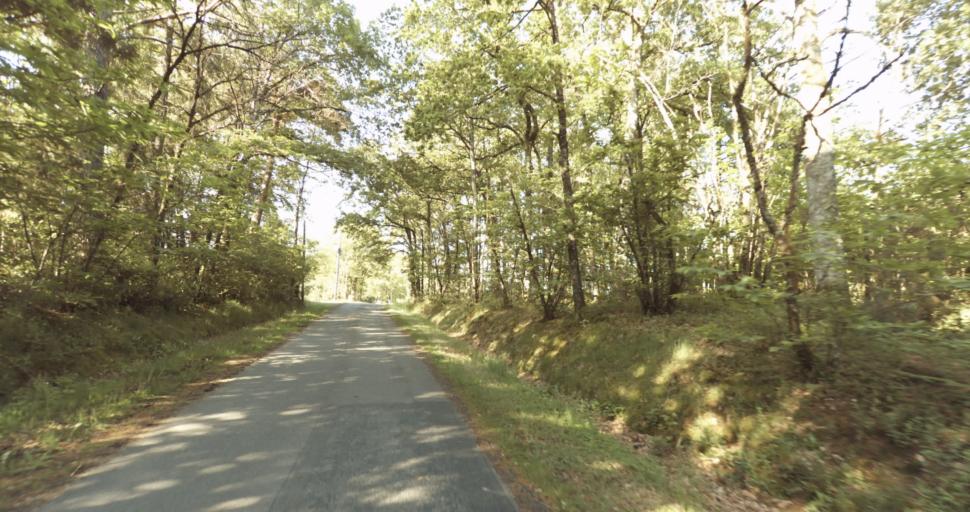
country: FR
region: Limousin
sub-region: Departement de la Haute-Vienne
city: Solignac
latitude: 45.7371
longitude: 1.2626
